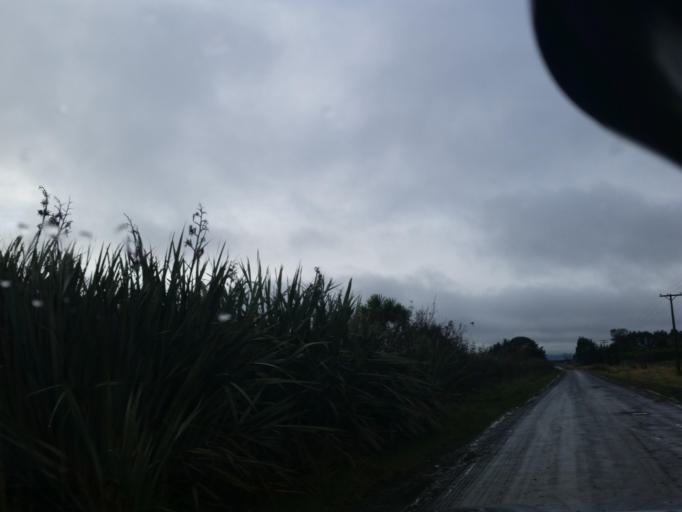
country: NZ
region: Southland
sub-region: Southland District
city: Winton
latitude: -46.2055
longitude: 168.2084
